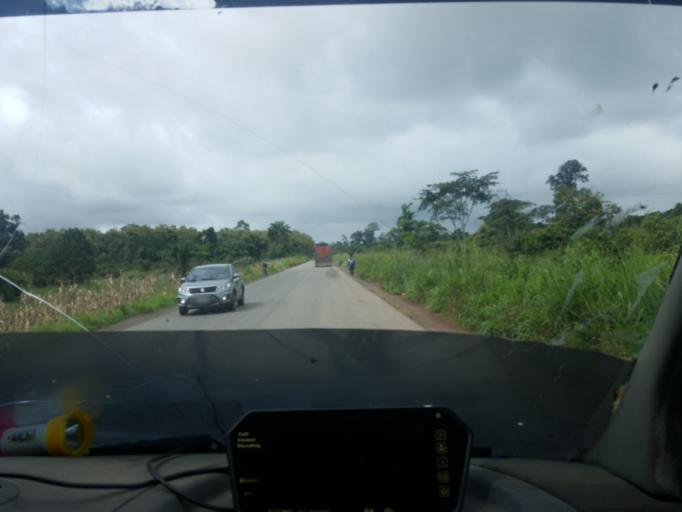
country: CI
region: Bas-Sassandra
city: Soubre
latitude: 5.7115
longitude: -6.6354
